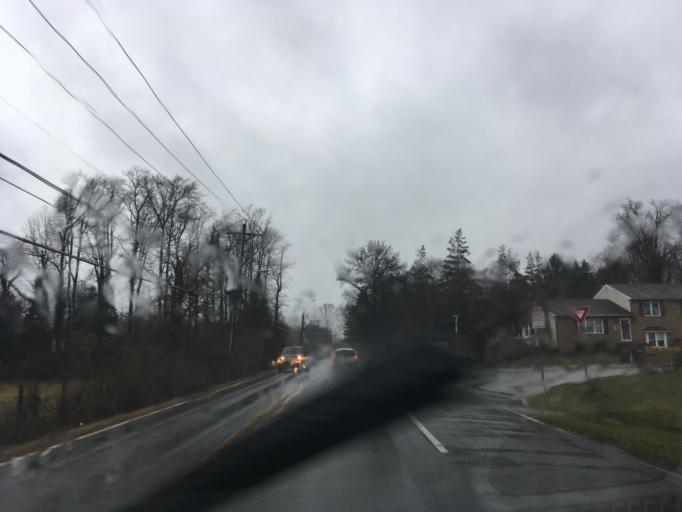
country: US
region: Delaware
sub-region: New Castle County
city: Bellefonte
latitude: 39.8254
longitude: -75.5254
